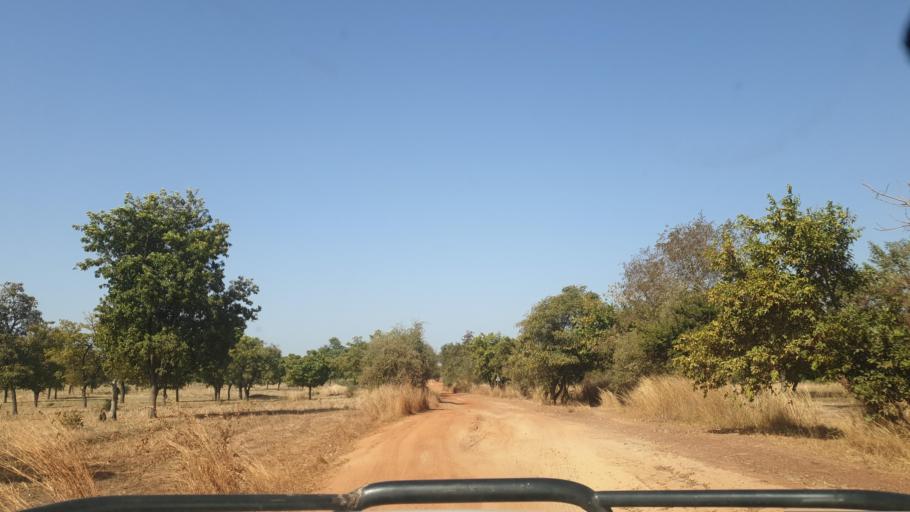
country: ML
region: Sikasso
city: Bougouni
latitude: 11.8213
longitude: -6.9679
